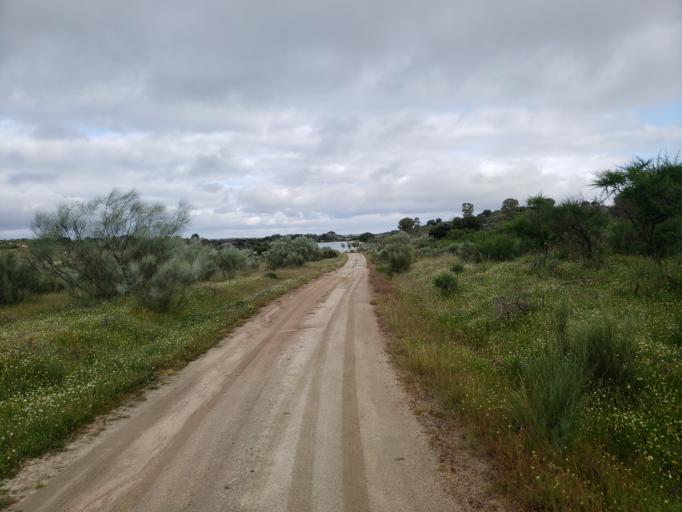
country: ES
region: Extremadura
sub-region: Provincia de Caceres
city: Malpartida de Caceres
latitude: 39.4249
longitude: -6.4830
